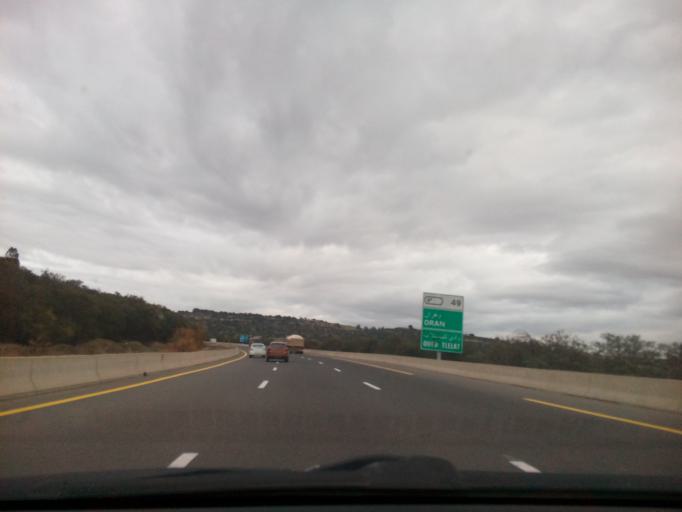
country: DZ
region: Sidi Bel Abbes
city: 'Ain el Berd
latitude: 35.3869
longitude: -0.4919
